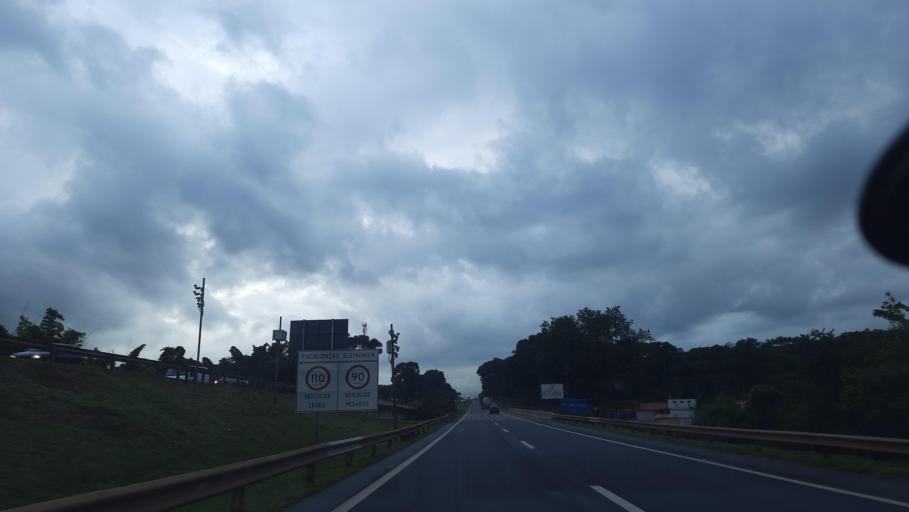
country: BR
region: Sao Paulo
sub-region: Moji-Guacu
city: Mogi-Gaucu
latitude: -22.3632
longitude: -46.9699
